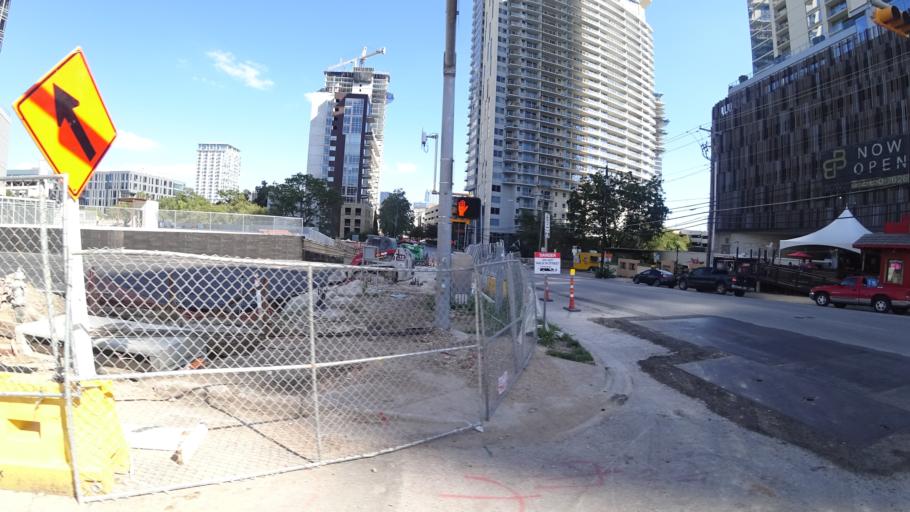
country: US
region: Texas
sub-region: Travis County
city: Austin
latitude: 30.2698
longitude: -97.7531
